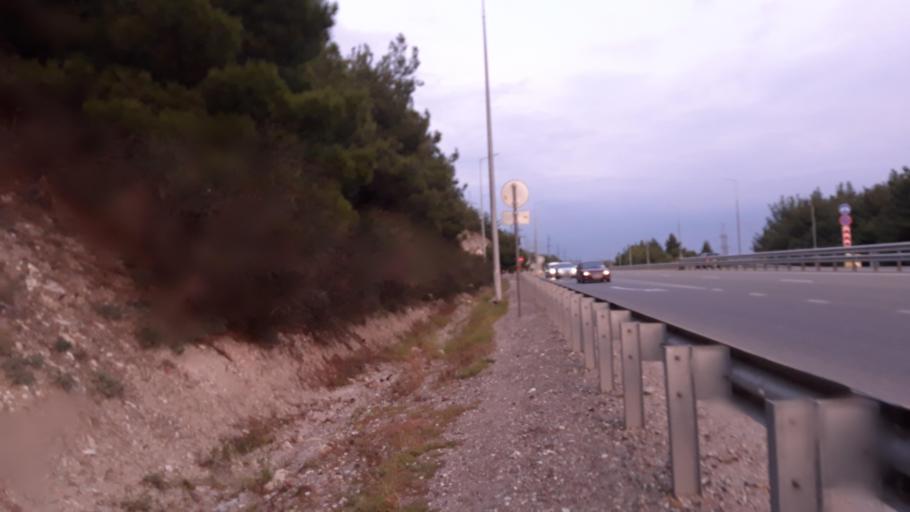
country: RU
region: Krasnodarskiy
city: Gelendzhik
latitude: 44.5779
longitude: 38.0889
